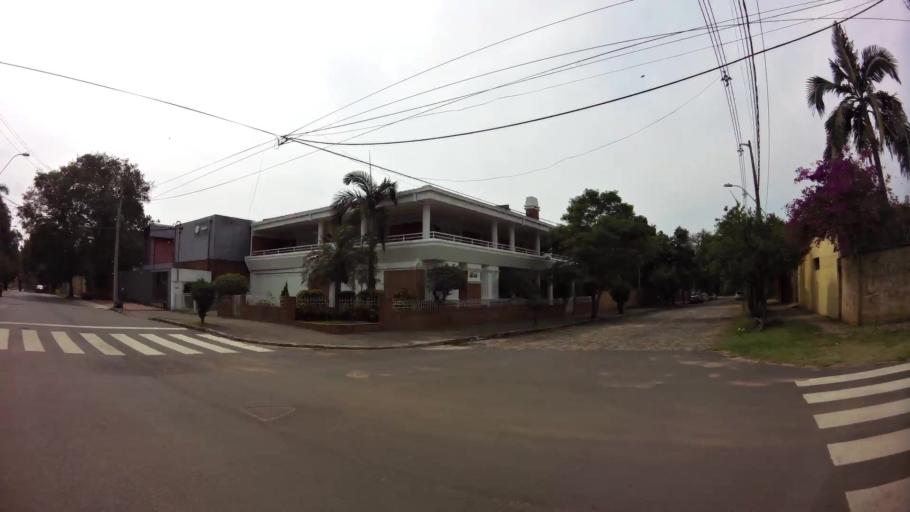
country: PY
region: Central
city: Fernando de la Mora
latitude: -25.2890
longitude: -57.5607
